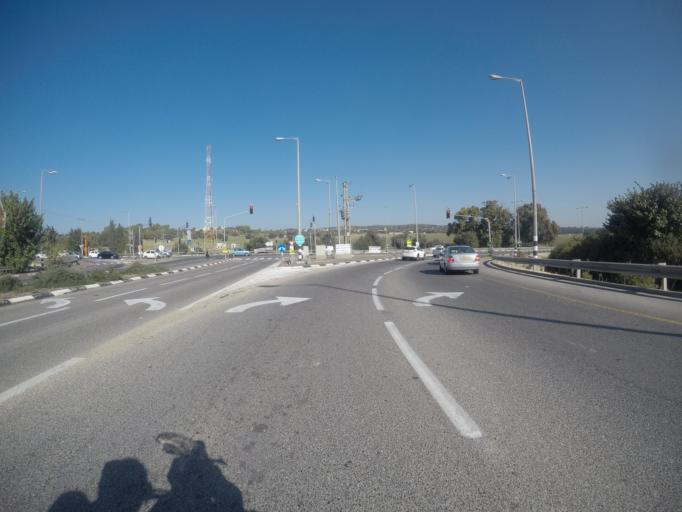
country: IL
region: Northern District
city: Ramat Yishay
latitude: 32.7091
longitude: 35.1365
